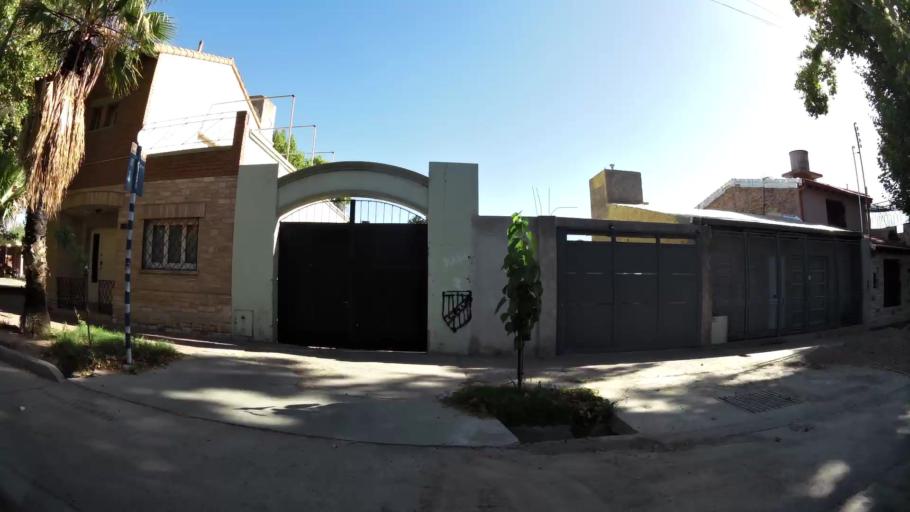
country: AR
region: Mendoza
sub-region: Departamento de Godoy Cruz
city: Godoy Cruz
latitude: -32.9245
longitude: -68.8617
